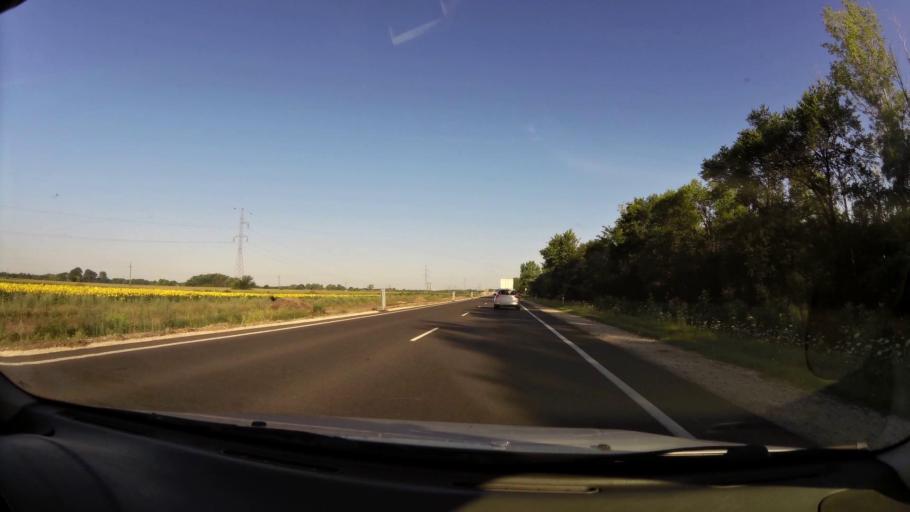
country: HU
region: Pest
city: Cegled
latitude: 47.2095
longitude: 19.7539
